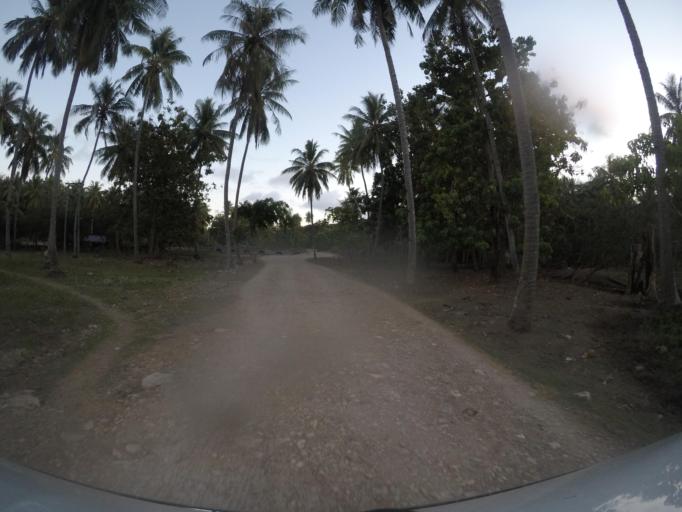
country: TL
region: Viqueque
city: Viqueque
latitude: -8.7791
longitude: 126.6364
